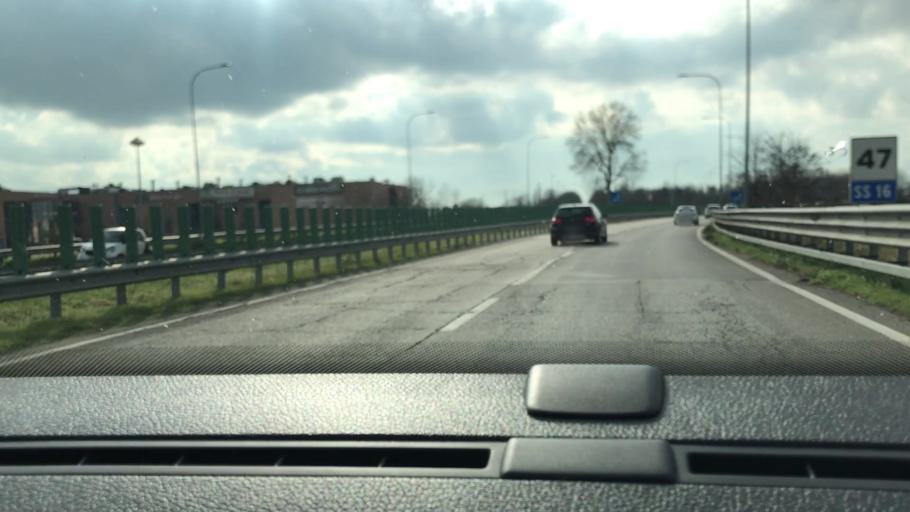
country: IT
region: Veneto
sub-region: Provincia di Rovigo
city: Grignano Polesine
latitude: 45.0303
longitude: 11.7768
